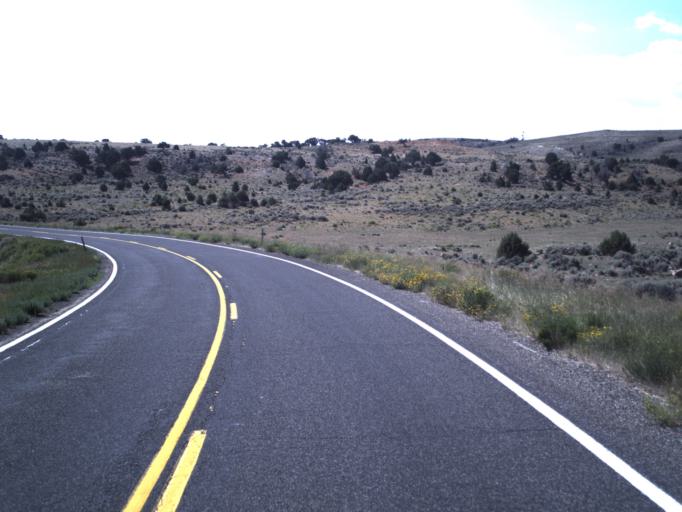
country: US
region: Utah
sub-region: Daggett County
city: Manila
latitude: 40.9840
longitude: -109.8423
